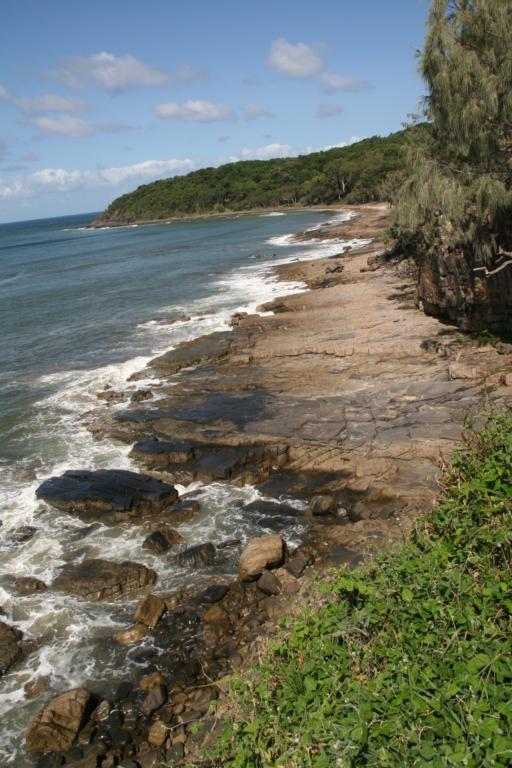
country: AU
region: Queensland
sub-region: Sunshine Coast
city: Noosa Heads
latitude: -26.3798
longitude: 153.1011
